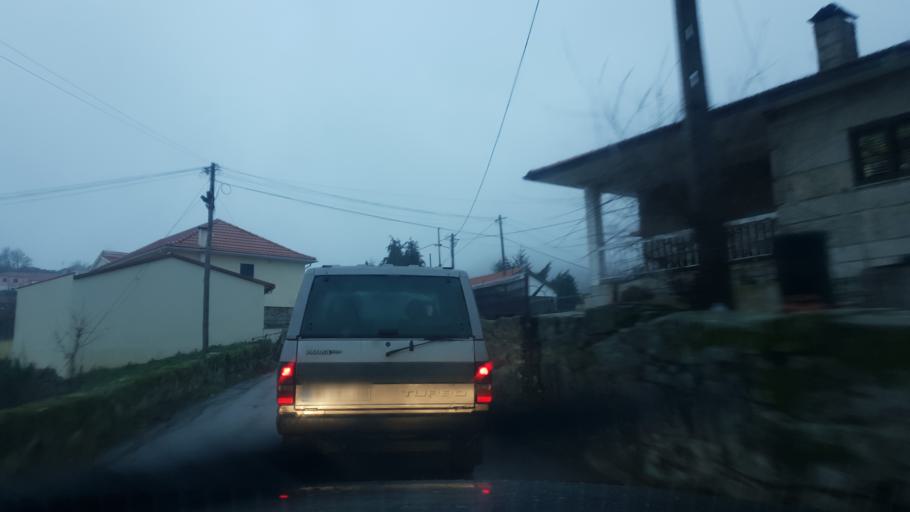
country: PT
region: Viseu
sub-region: Oliveira de Frades
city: Oliveira de Frades
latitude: 40.8276
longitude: -8.1475
